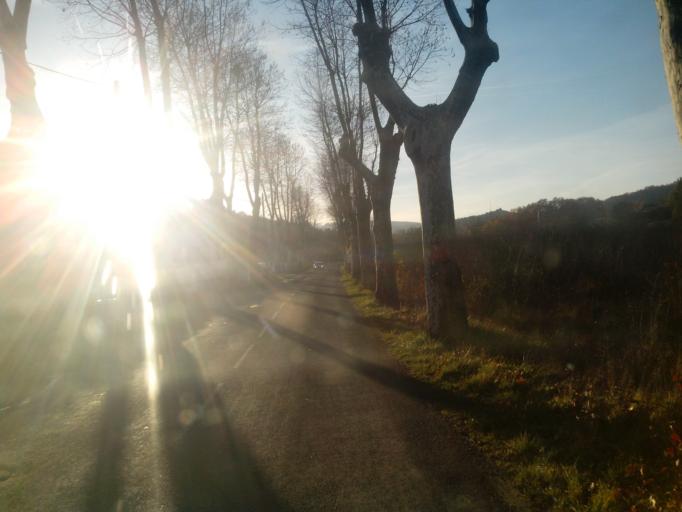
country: FR
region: Languedoc-Roussillon
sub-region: Departement de l'Aude
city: Couiza
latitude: 42.9417
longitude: 2.2475
